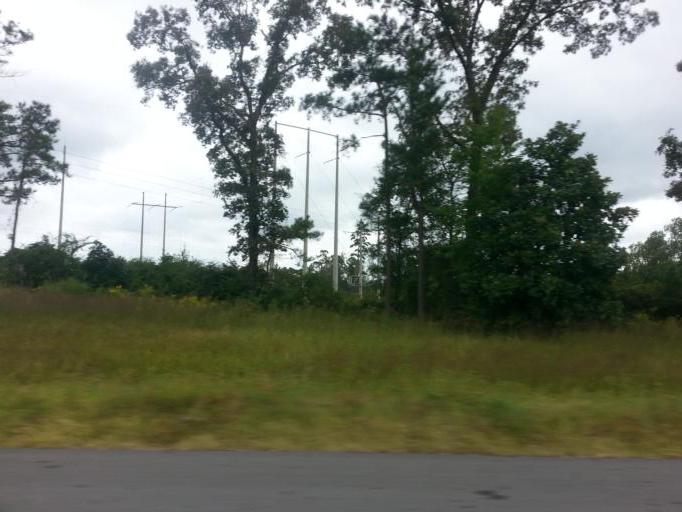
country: US
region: Alabama
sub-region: Conecuh County
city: Evergreen
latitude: 31.3417
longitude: -87.1034
